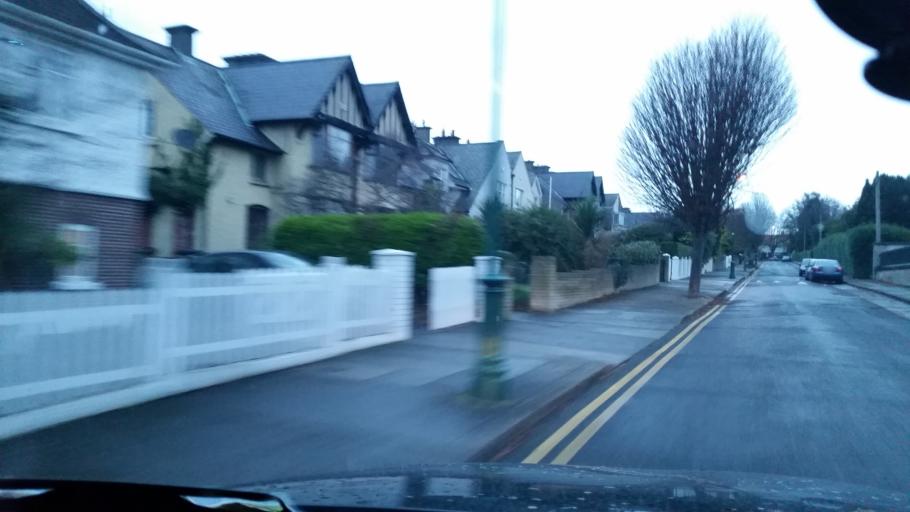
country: IE
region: Leinster
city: Drumcondra
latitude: 53.3750
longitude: -6.2579
